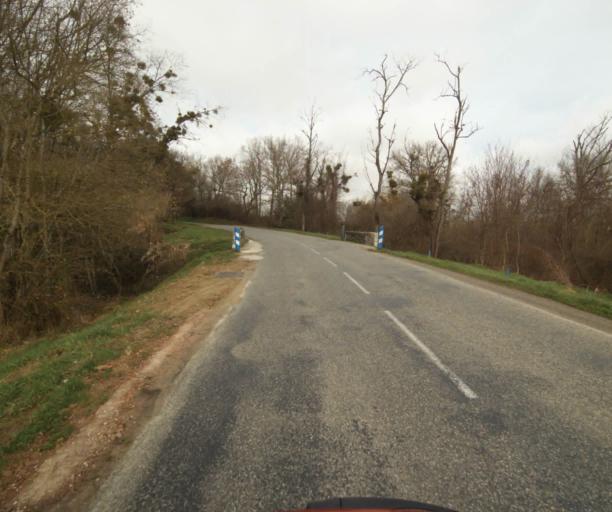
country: FR
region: Midi-Pyrenees
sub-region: Departement de l'Ariege
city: Pamiers
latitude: 43.1104
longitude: 1.5475
